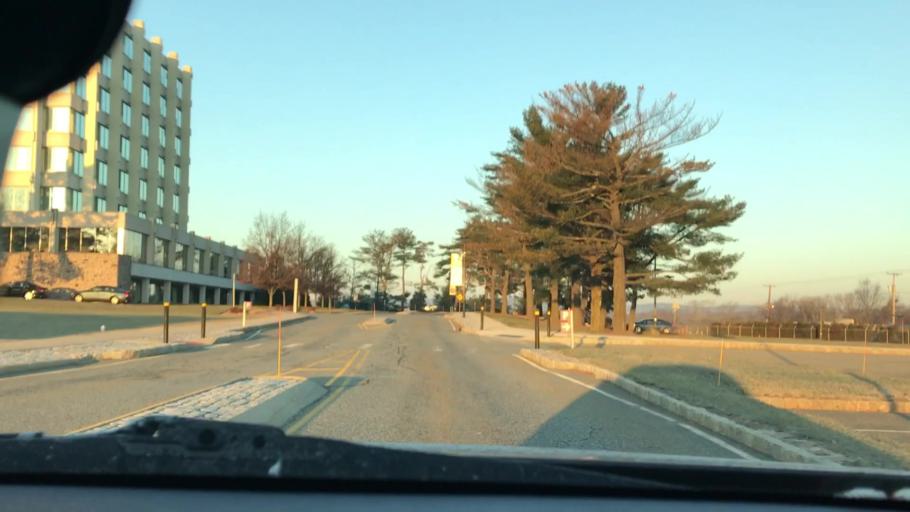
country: US
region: New Jersey
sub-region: Morris County
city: Hanover
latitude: 40.8115
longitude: -74.3890
